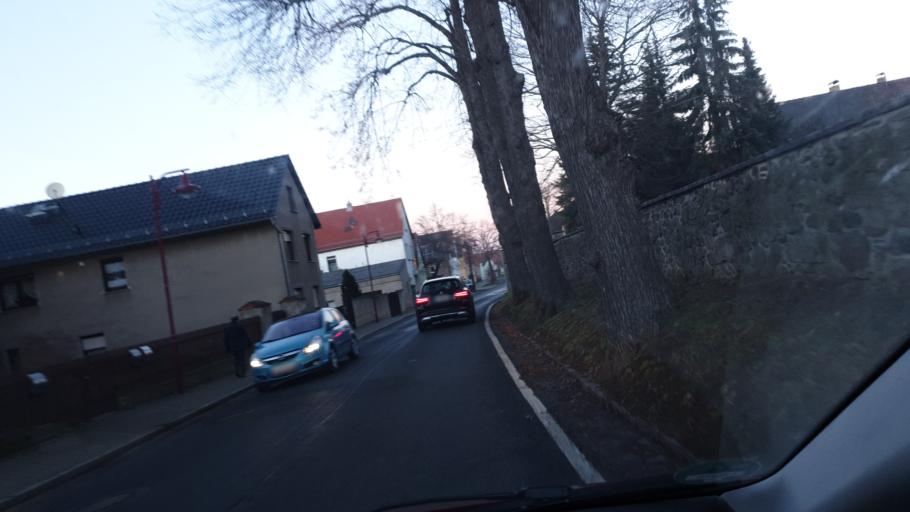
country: DE
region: Saxony
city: Hohburg
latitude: 51.4539
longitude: 12.7820
